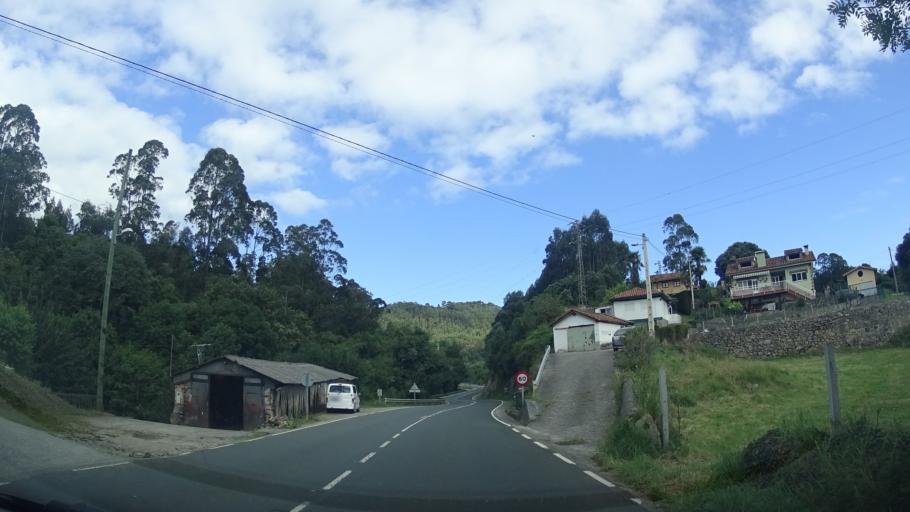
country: ES
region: Asturias
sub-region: Province of Asturias
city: Ribadesella
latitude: 43.4648
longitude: -5.1278
